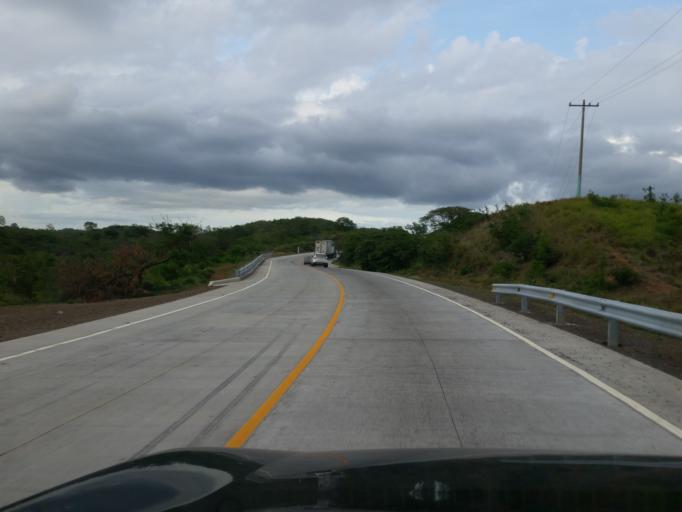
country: NI
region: Managua
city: Carlos Fonseca Amador
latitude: 12.0737
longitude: -86.4308
